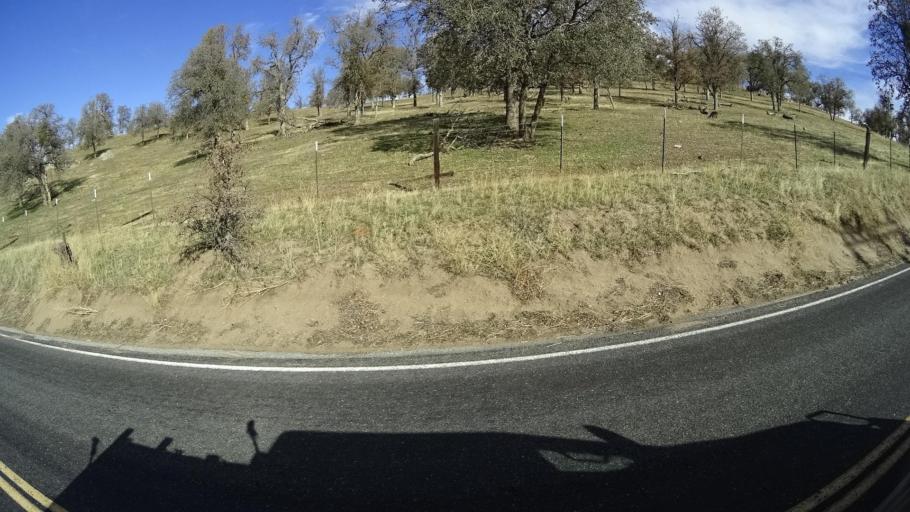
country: US
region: California
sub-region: Kern County
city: Alta Sierra
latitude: 35.6459
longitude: -118.7866
